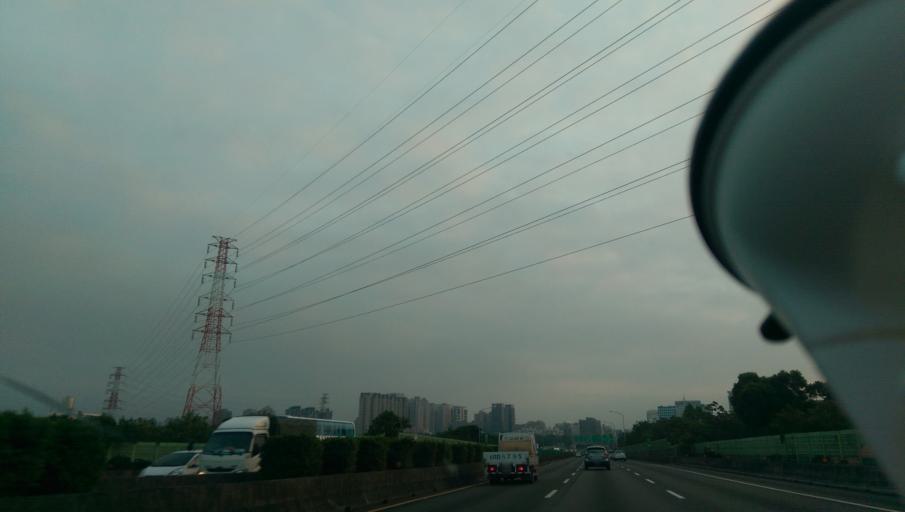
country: TW
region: Taiwan
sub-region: Hsinchu
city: Zhubei
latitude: 24.8071
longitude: 121.0101
